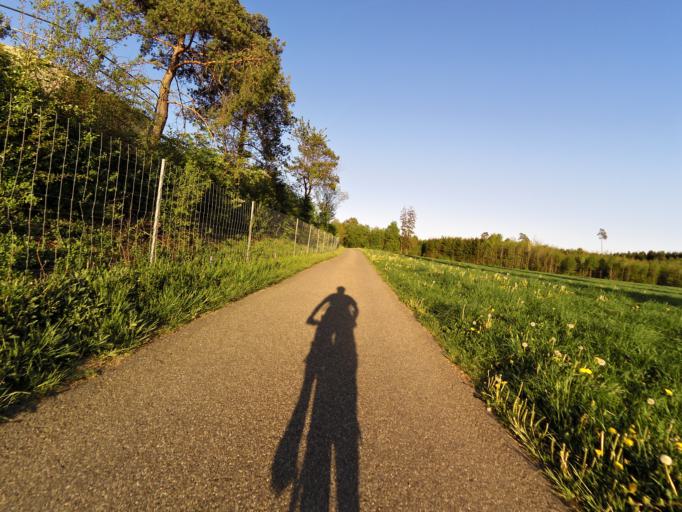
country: CH
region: Zurich
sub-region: Bezirk Winterthur
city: Oberwinterthur (Kreis 2) / Zinzikon
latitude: 47.5281
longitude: 8.7602
